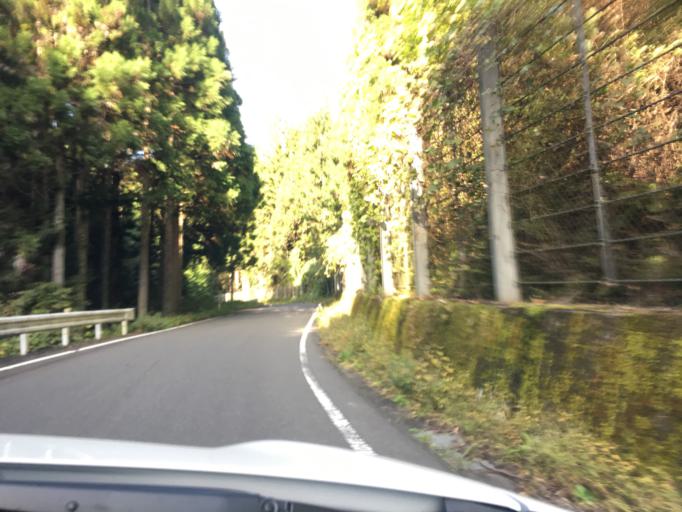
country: JP
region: Fukushima
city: Ishikawa
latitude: 37.1215
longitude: 140.5582
